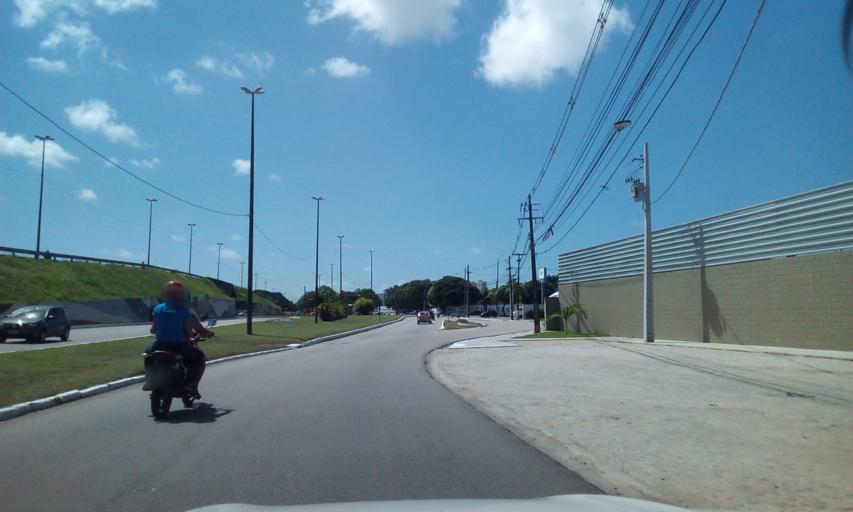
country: BR
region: Paraiba
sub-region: Joao Pessoa
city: Joao Pessoa
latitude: -7.1667
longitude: -34.8632
